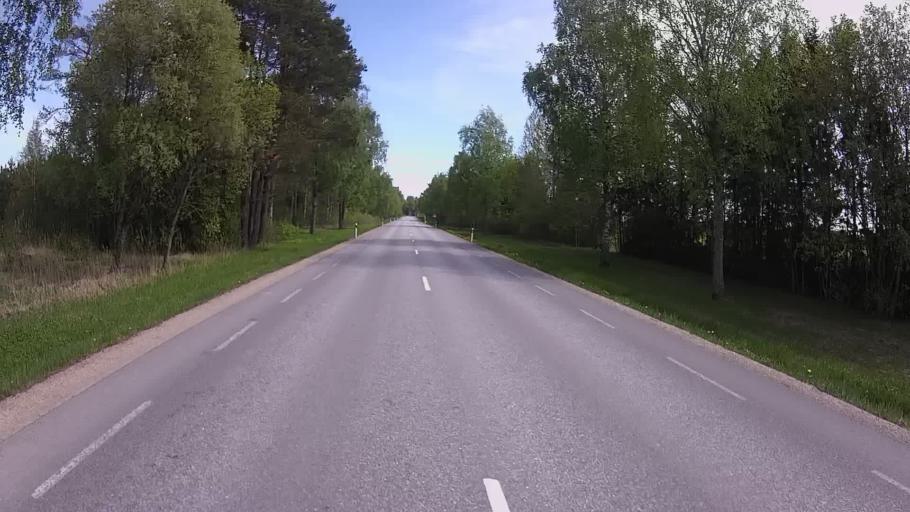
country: EE
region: Valgamaa
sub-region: Valga linn
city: Valga
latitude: 57.7304
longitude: 26.1661
